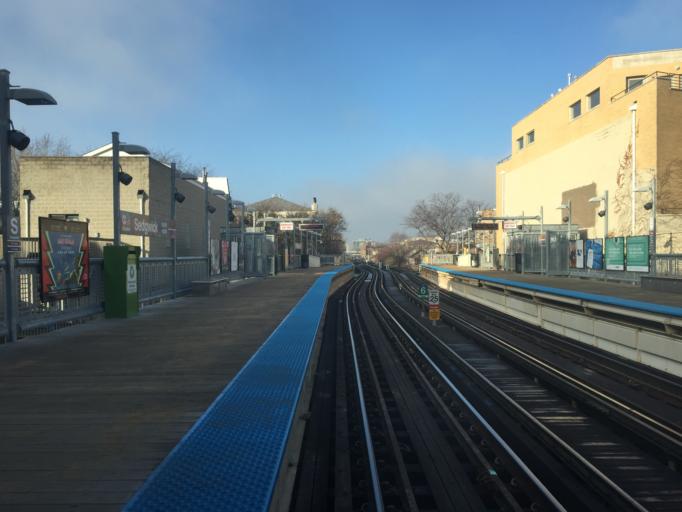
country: US
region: Illinois
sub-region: Cook County
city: Chicago
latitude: 41.9104
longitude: -87.6391
